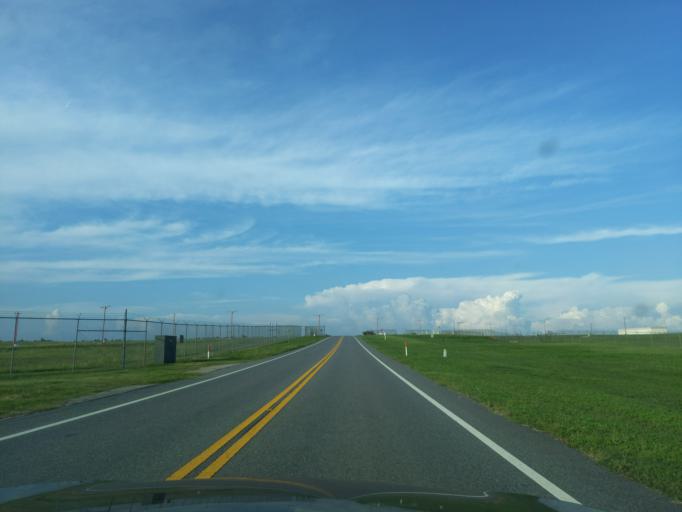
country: US
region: Florida
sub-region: Leon County
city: Tallahassee
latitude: 30.3905
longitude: -84.3263
